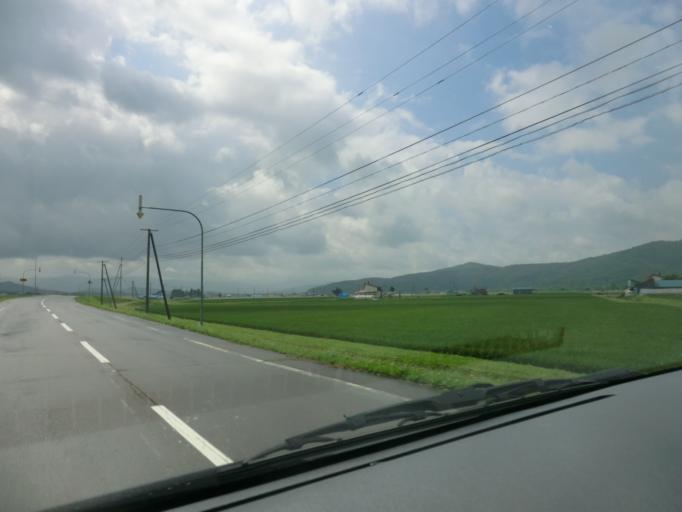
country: JP
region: Hokkaido
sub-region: Asahikawa-shi
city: Asahikawa
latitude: 44.0486
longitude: 142.1462
